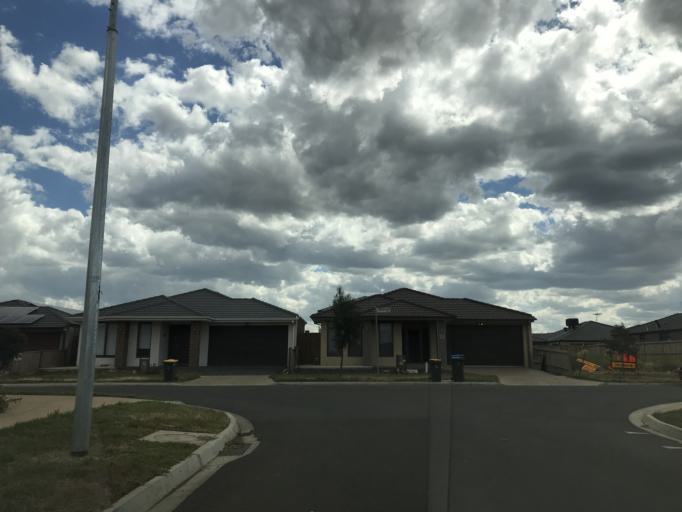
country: AU
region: Victoria
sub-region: Wyndham
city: Truganina
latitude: -37.8204
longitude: 144.7138
